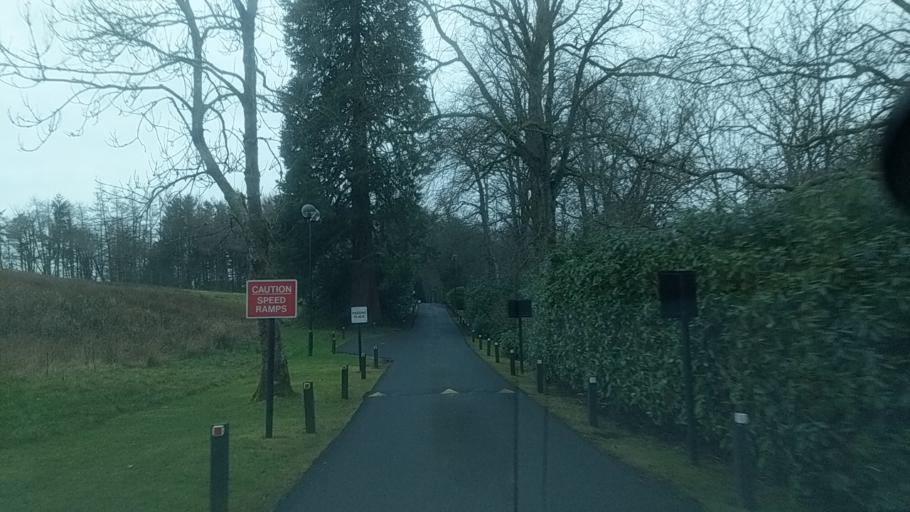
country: GB
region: Scotland
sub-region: South Lanarkshire
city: East Kilbride
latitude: 55.7393
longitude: -4.1493
